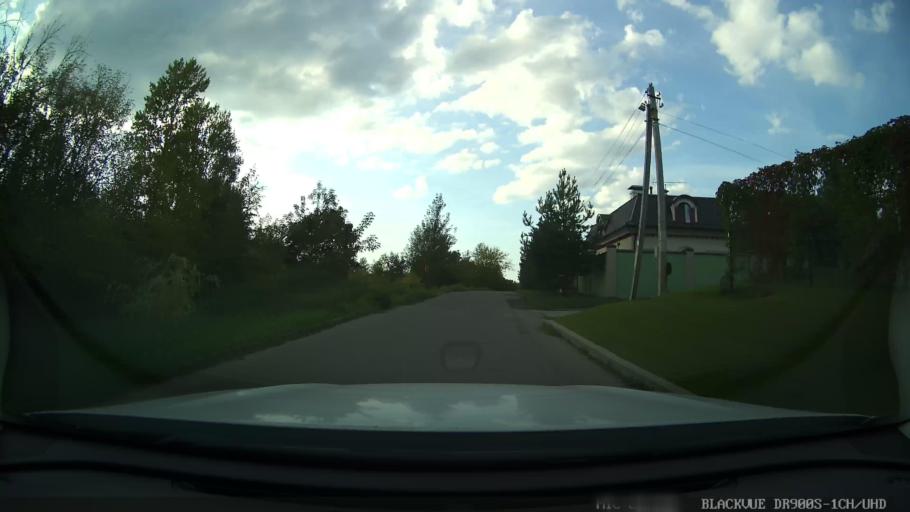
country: RU
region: Moskovskaya
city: Nemchinovka
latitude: 55.7388
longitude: 37.3425
